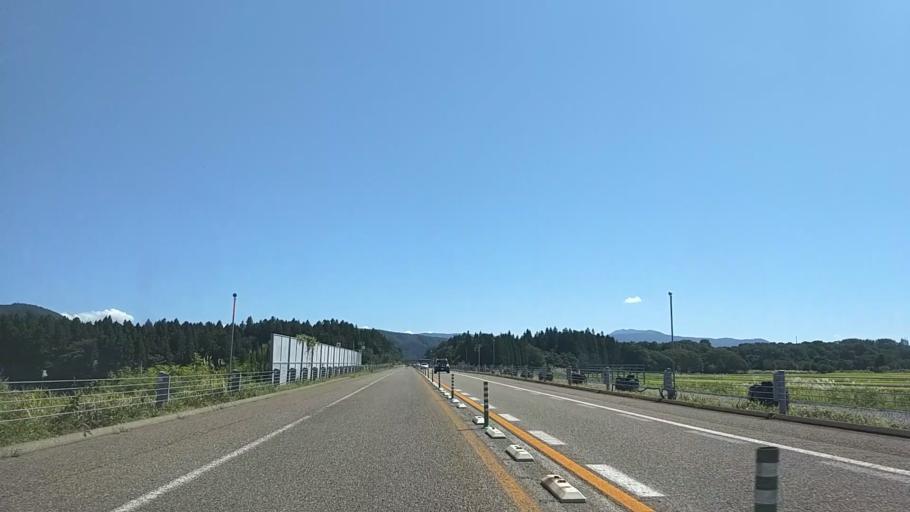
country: JP
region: Niigata
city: Arai
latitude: 36.9899
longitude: 138.2074
